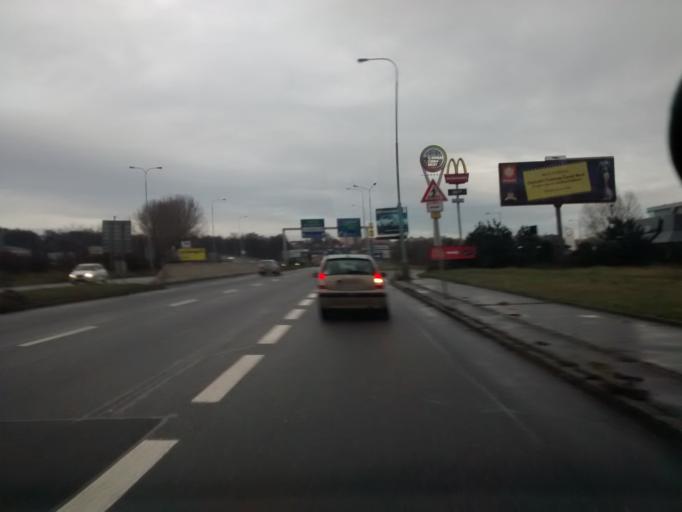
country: CZ
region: Praha
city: Cerny Most
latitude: 50.1099
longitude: 14.5821
